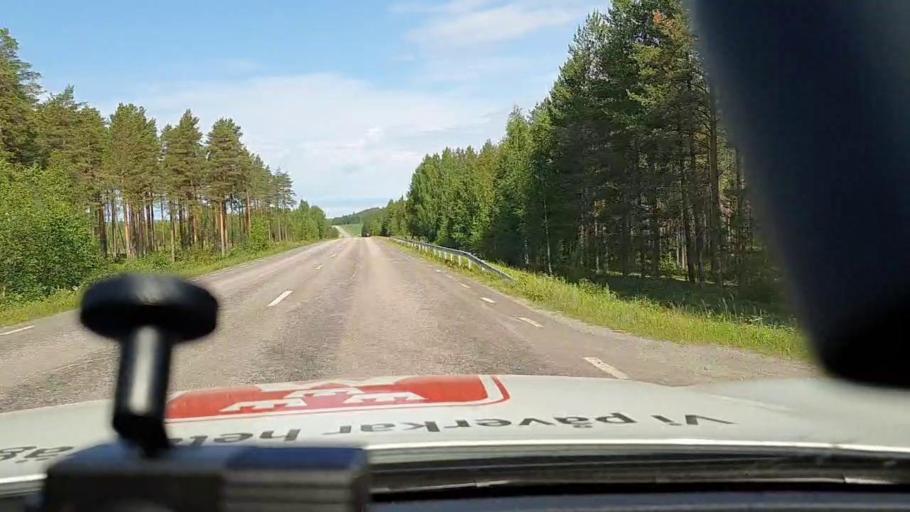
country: SE
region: Norrbotten
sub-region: Bodens Kommun
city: Boden
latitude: 65.9071
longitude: 21.3590
